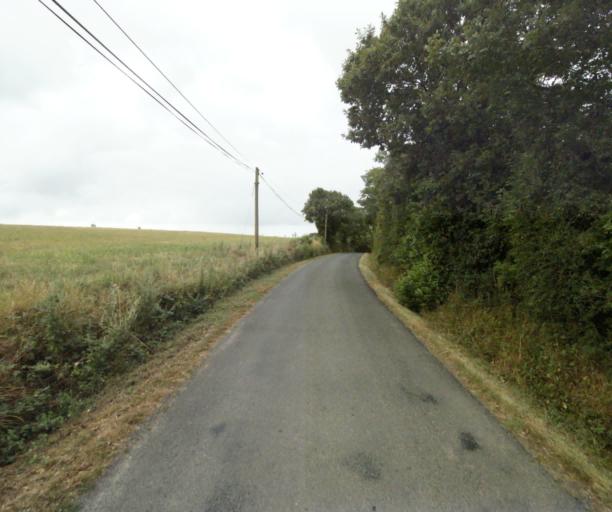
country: FR
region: Midi-Pyrenees
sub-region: Departement du Tarn
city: Soreze
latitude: 43.3980
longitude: 2.0575
